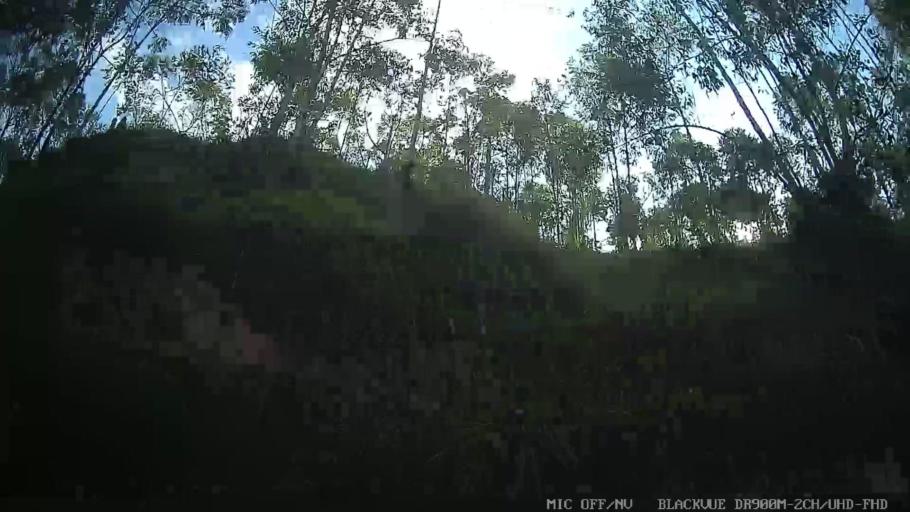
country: BR
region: Sao Paulo
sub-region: Serra Negra
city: Serra Negra
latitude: -22.6445
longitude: -46.6968
